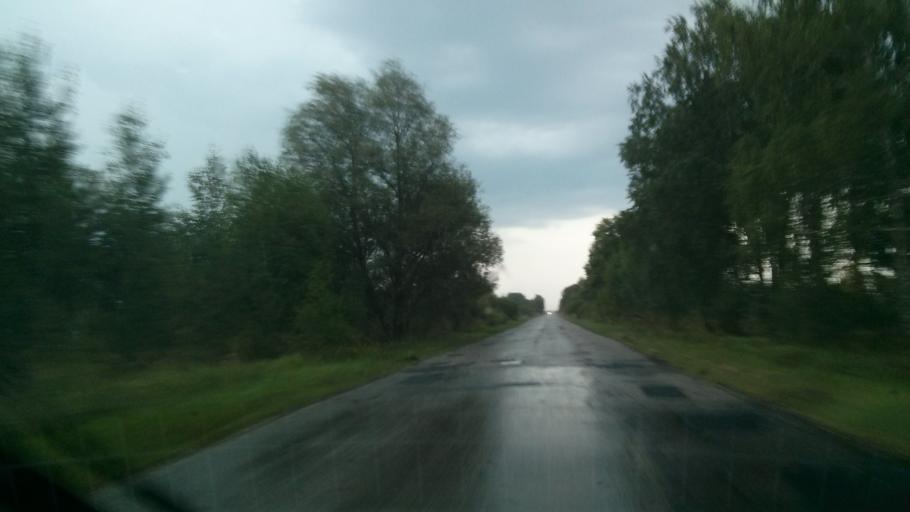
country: RU
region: Nizjnij Novgorod
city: Shimorskoye
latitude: 55.3376
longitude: 41.8941
